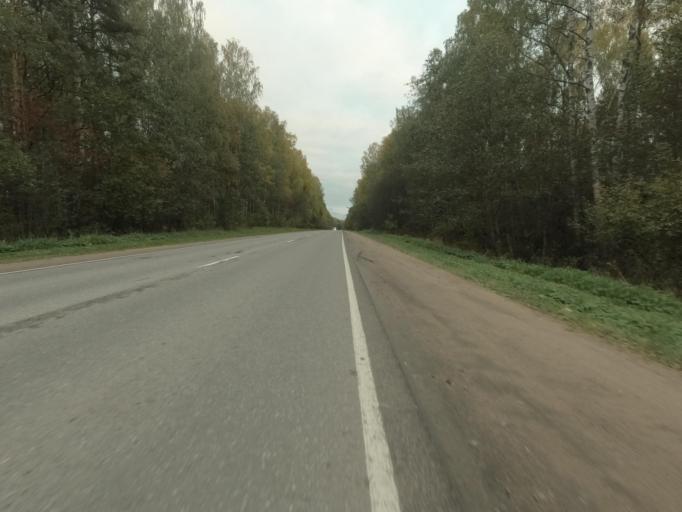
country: RU
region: Leningrad
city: Pavlovo
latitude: 59.8095
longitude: 30.9273
